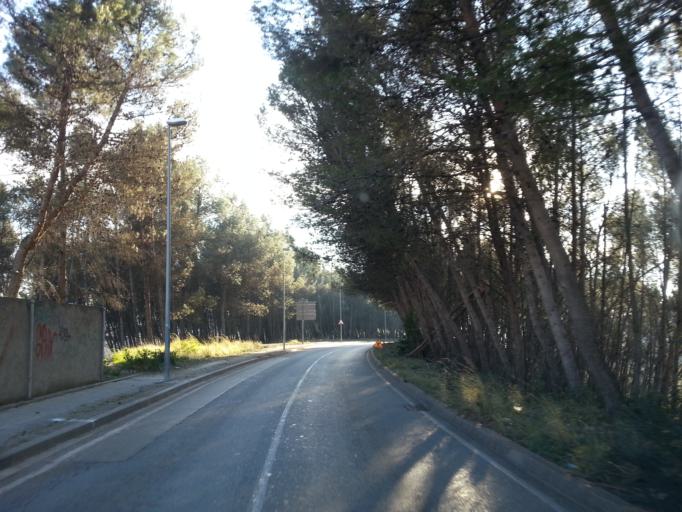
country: ES
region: Catalonia
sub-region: Provincia de Barcelona
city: Terrassa
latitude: 41.5666
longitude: 1.9955
